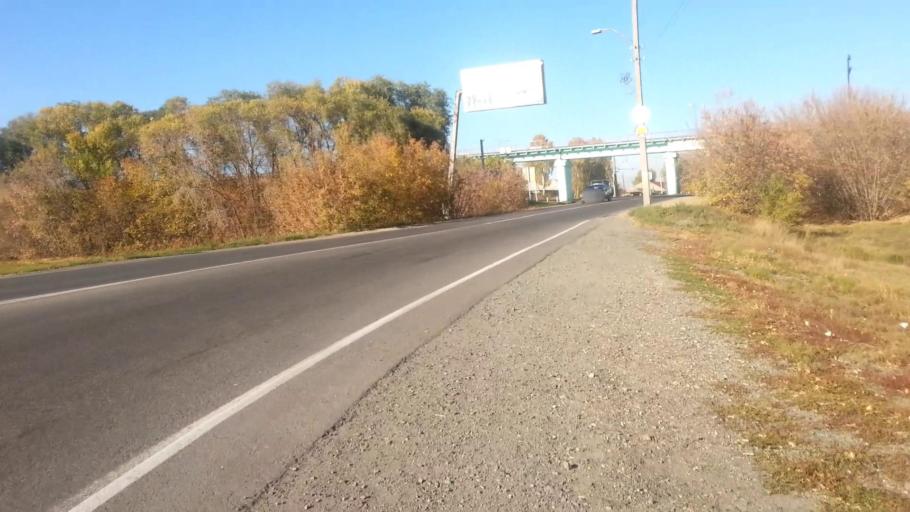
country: RU
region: Altai Krai
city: Novoaltaysk
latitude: 53.3745
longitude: 83.9348
